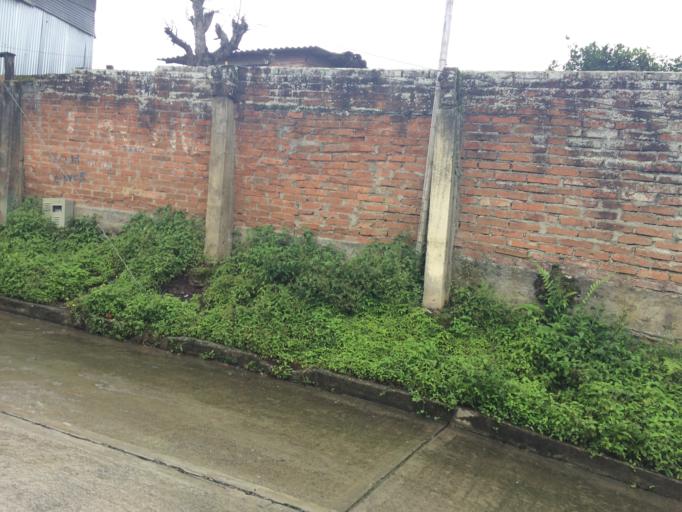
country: CO
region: Quindio
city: Genova
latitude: 4.2086
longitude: -75.7889
